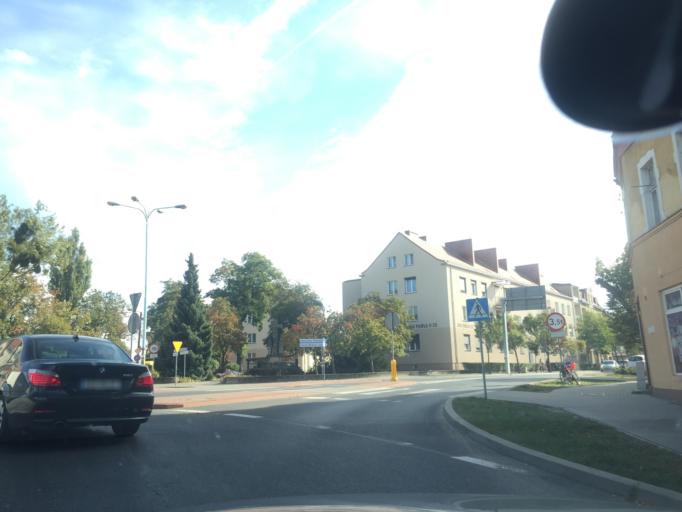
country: PL
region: Greater Poland Voivodeship
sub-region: Powiat wrzesinski
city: Wrzesnia
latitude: 52.3291
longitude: 17.5632
